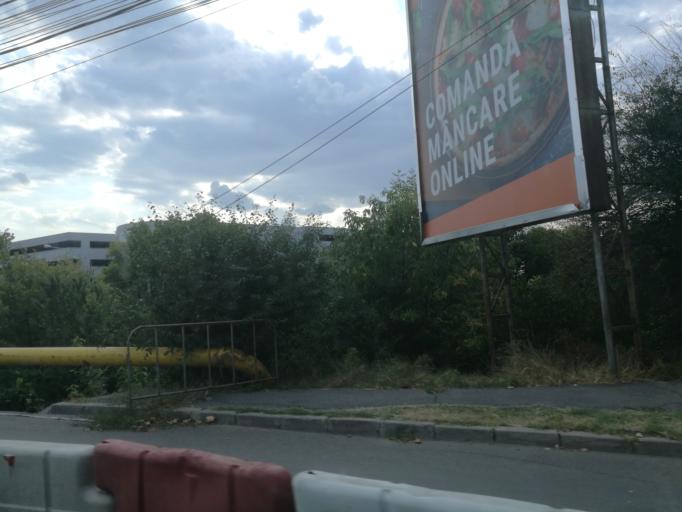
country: RO
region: Ilfov
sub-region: Comuna Mogosoaia
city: Mogosoaia
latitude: 44.5043
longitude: 26.0252
